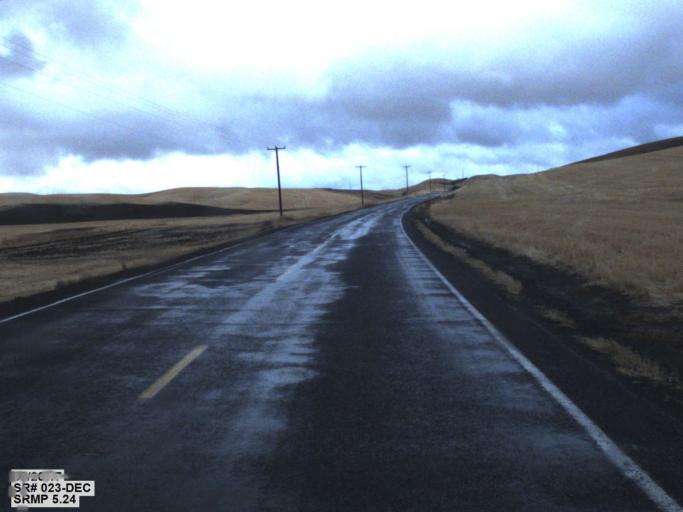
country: US
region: Washington
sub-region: Whitman County
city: Colfax
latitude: 47.0086
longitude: -117.4596
